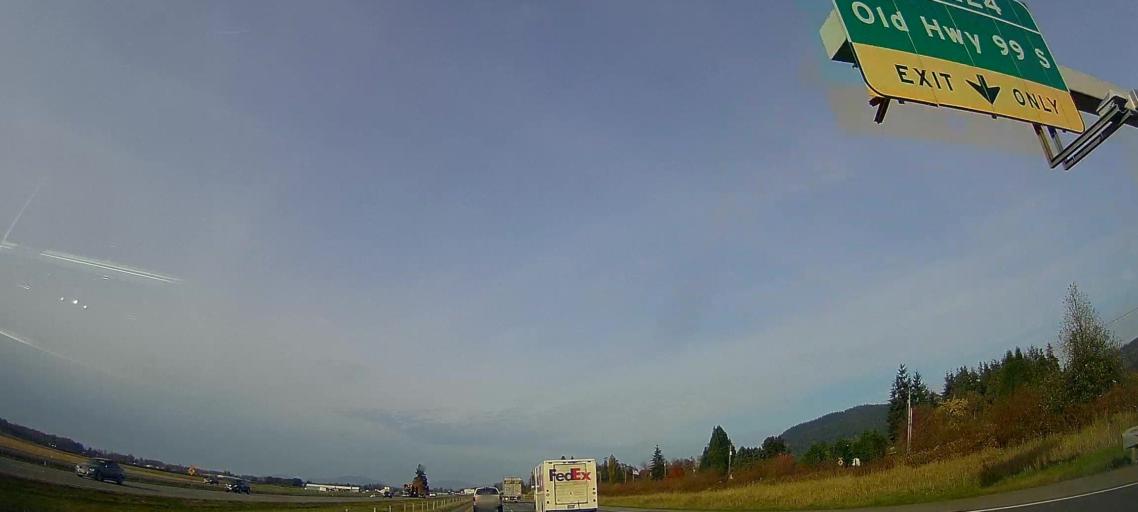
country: US
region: Washington
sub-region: Skagit County
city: Mount Vernon
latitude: 48.3693
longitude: -122.3346
